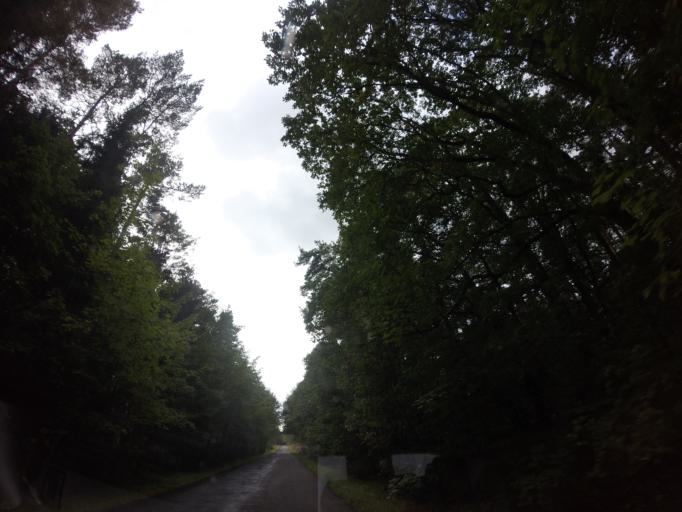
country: PL
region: West Pomeranian Voivodeship
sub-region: Powiat goleniowski
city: Przybiernow
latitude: 53.6985
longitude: 14.7099
